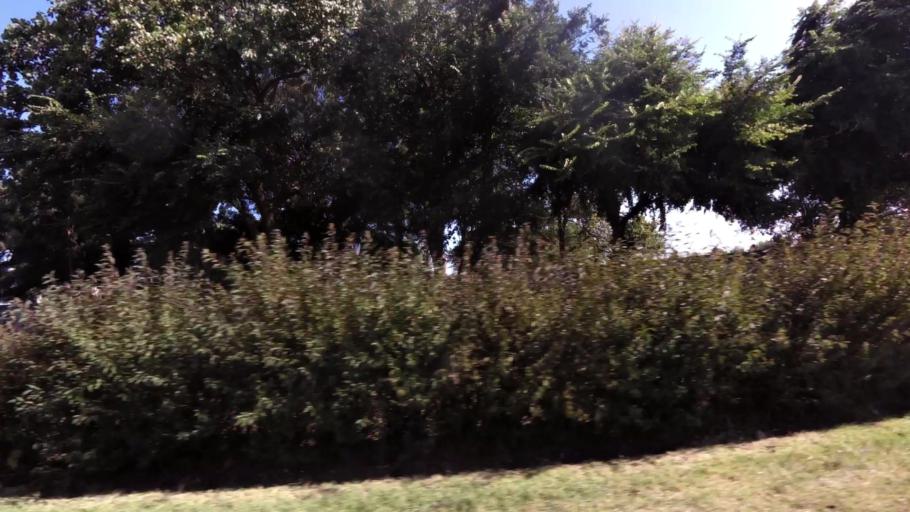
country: CL
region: Biobio
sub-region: Provincia de Concepcion
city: Talcahuano
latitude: -36.7809
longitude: -73.0937
